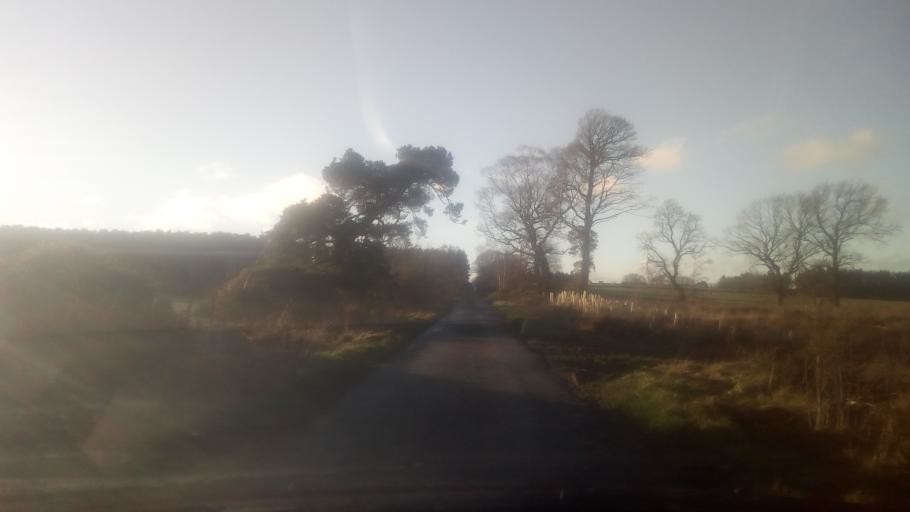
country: GB
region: Scotland
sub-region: The Scottish Borders
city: Jedburgh
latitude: 55.4708
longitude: -2.4444
